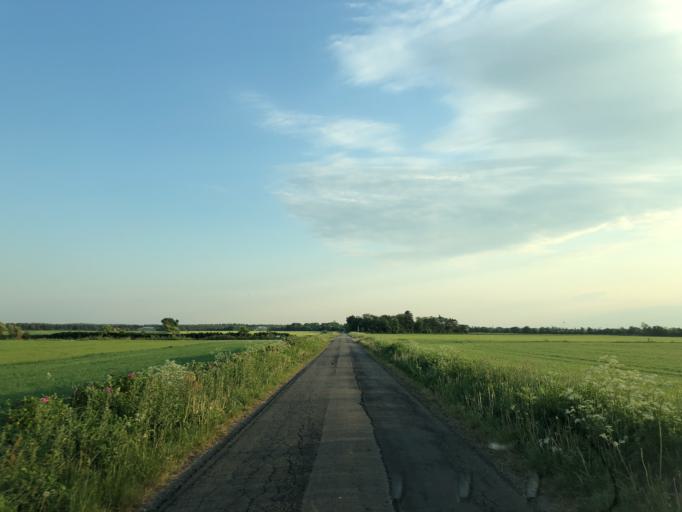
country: DK
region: Central Jutland
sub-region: Holstebro Kommune
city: Holstebro
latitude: 56.3828
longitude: 8.4660
